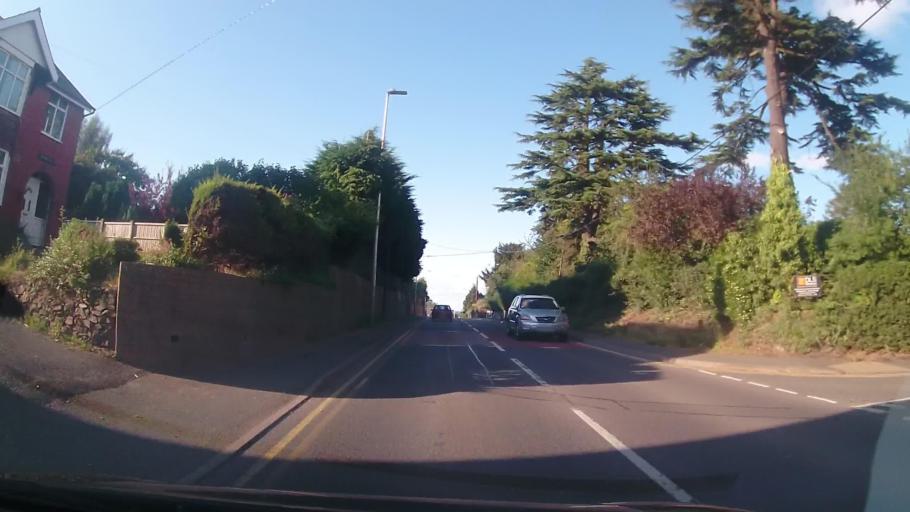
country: GB
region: England
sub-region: Shropshire
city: Bayston Hill
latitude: 52.6733
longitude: -2.7608
